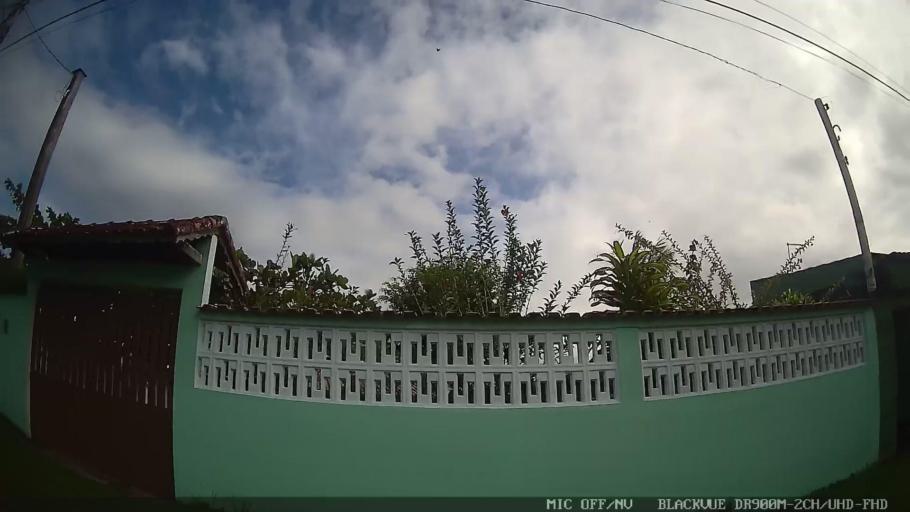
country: BR
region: Sao Paulo
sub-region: Itanhaem
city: Itanhaem
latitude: -24.2313
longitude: -46.8907
